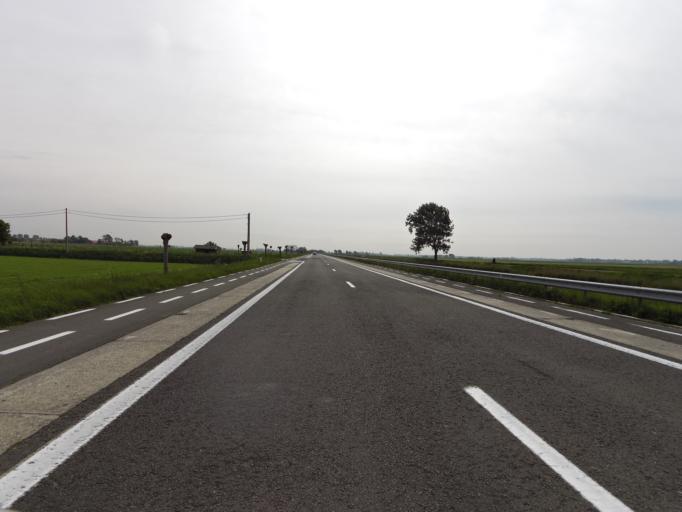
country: BE
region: Flanders
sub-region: Provincie West-Vlaanderen
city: Nieuwpoort
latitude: 51.1171
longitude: 2.7377
